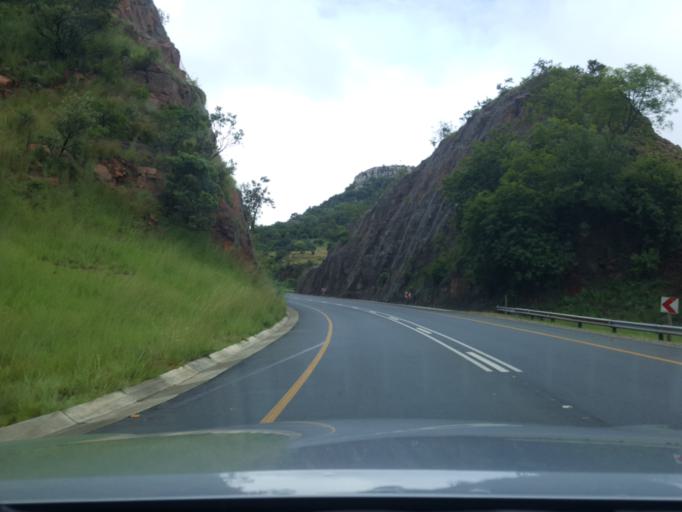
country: ZA
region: Mpumalanga
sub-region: Nkangala District Municipality
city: Belfast
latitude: -25.6457
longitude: 30.3585
